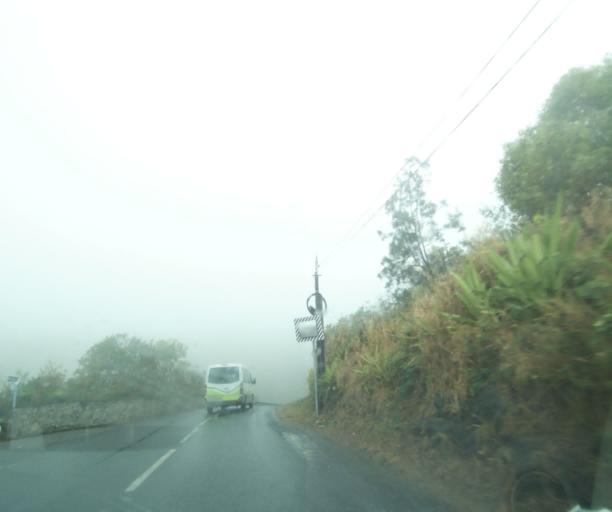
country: RE
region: Reunion
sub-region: Reunion
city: Saint-Paul
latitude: -21.0099
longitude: 55.3152
